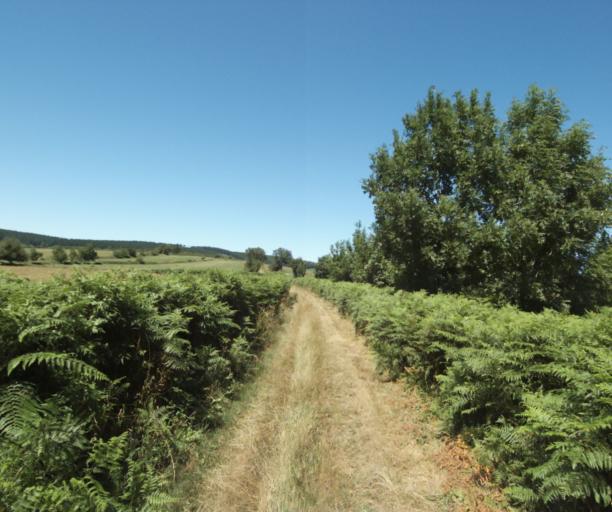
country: FR
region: Midi-Pyrenees
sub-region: Departement du Tarn
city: Dourgne
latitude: 43.4341
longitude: 2.1549
